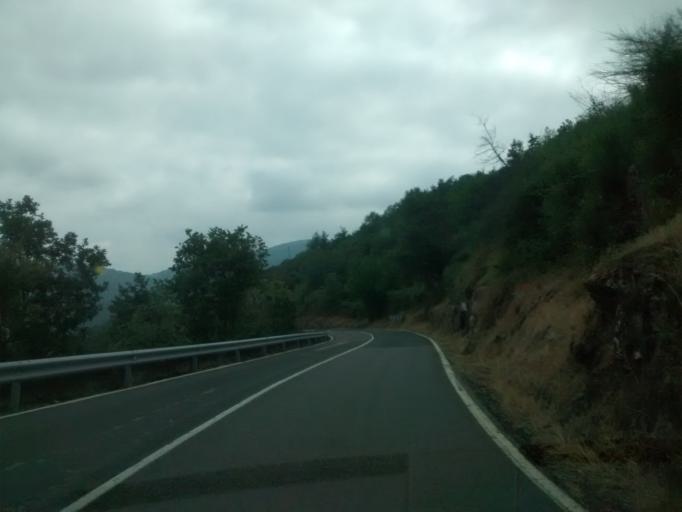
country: ES
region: Galicia
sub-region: Provincia de Ourense
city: Manzaneda
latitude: 42.3366
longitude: -7.2323
